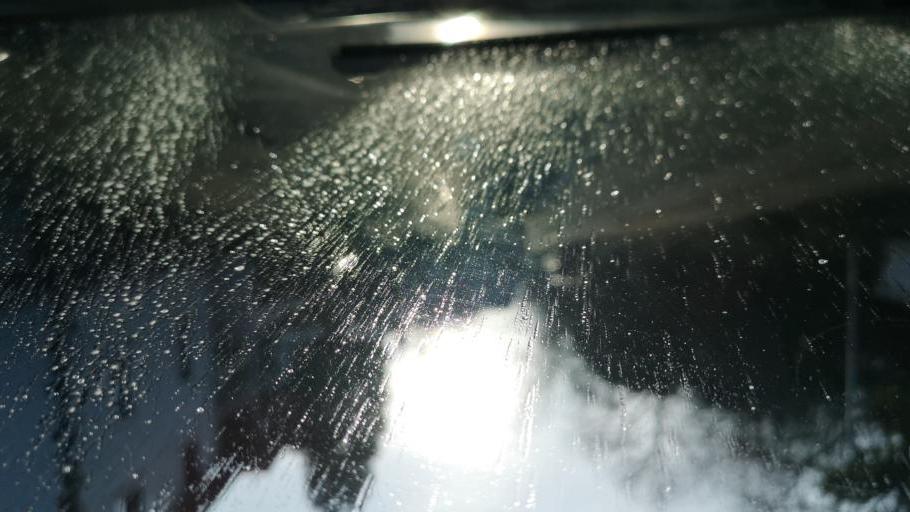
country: DE
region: Baden-Wuerttemberg
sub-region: Karlsruhe Region
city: Ettlingen
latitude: 48.9675
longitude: 8.4782
